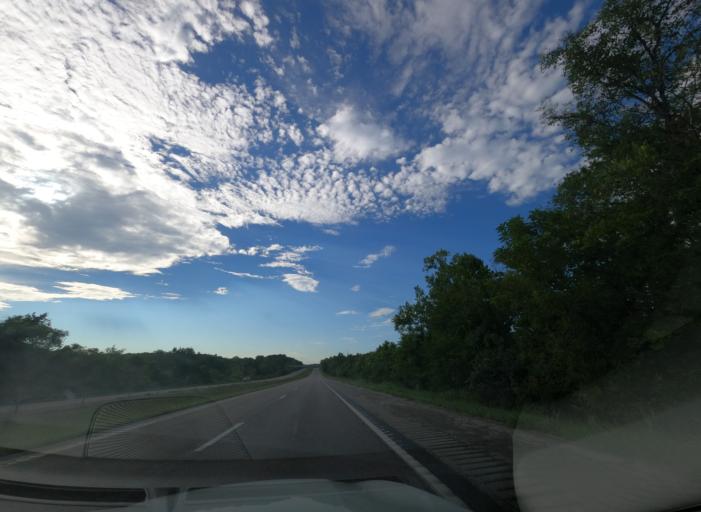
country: US
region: Missouri
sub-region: Jefferson County
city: Crystal City
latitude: 38.1363
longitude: -90.3242
